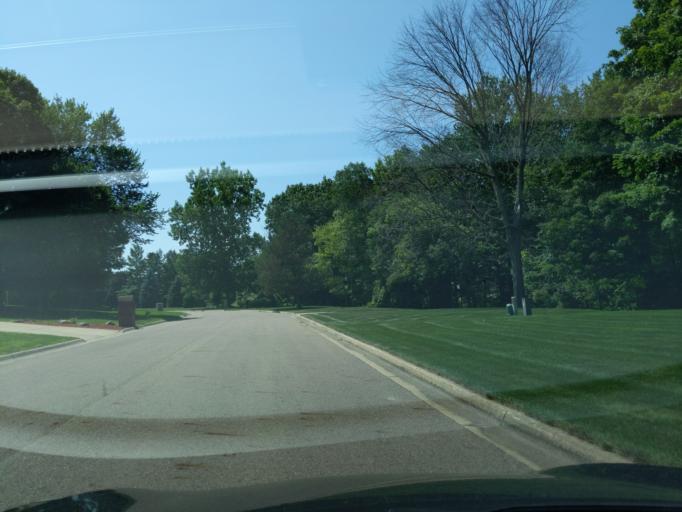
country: US
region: Michigan
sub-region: Ingham County
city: Edgemont Park
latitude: 42.7684
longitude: -84.6126
